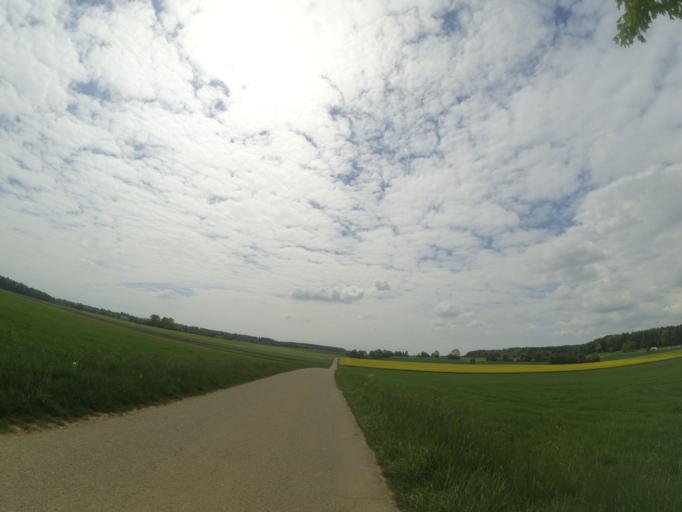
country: DE
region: Baden-Wuerttemberg
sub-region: Tuebingen Region
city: Berghulen
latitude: 48.4495
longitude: 9.7720
